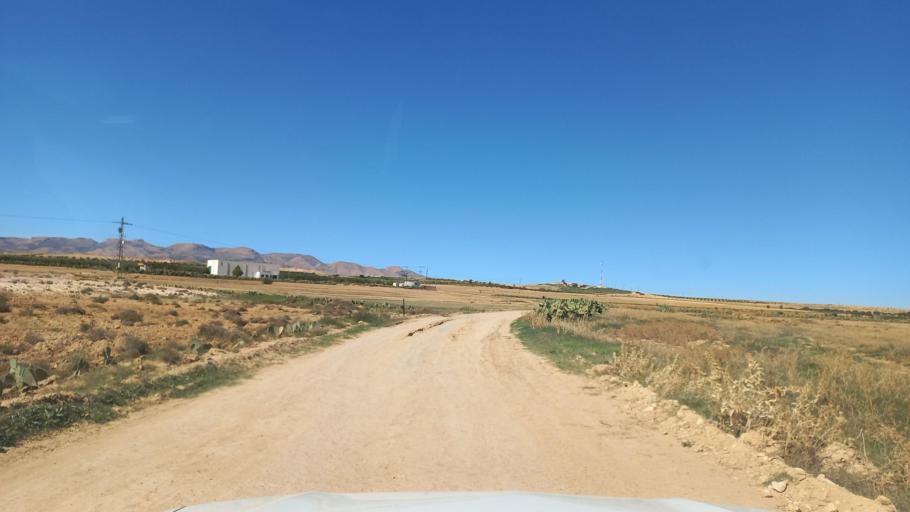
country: TN
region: Al Qasrayn
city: Sbiba
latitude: 35.3685
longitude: 9.0955
